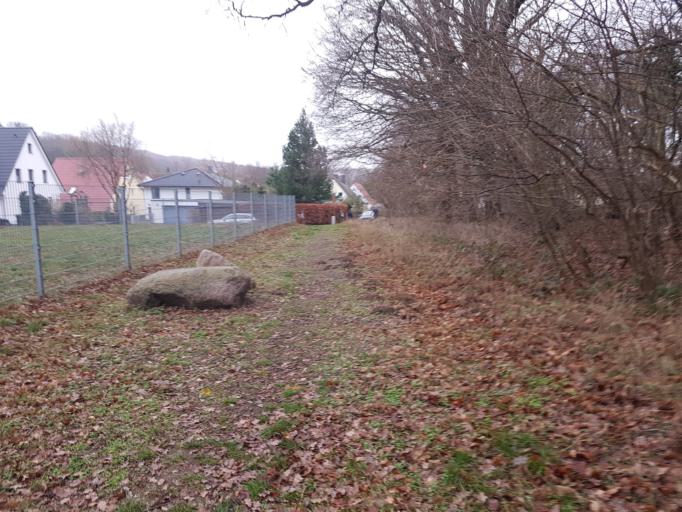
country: DE
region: Mecklenburg-Vorpommern
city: Ostseebad Binz
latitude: 54.3919
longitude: 13.6184
